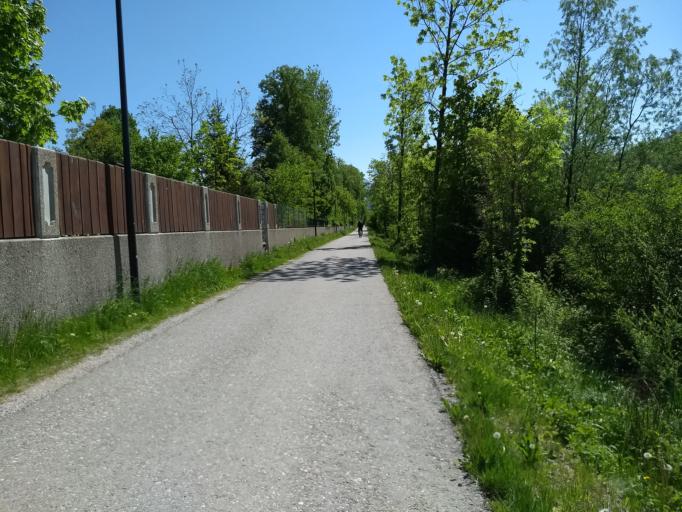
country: AT
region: Salzburg
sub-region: Politischer Bezirk Salzburg-Umgebung
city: Elsbethen
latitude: 47.7808
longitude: 13.0768
